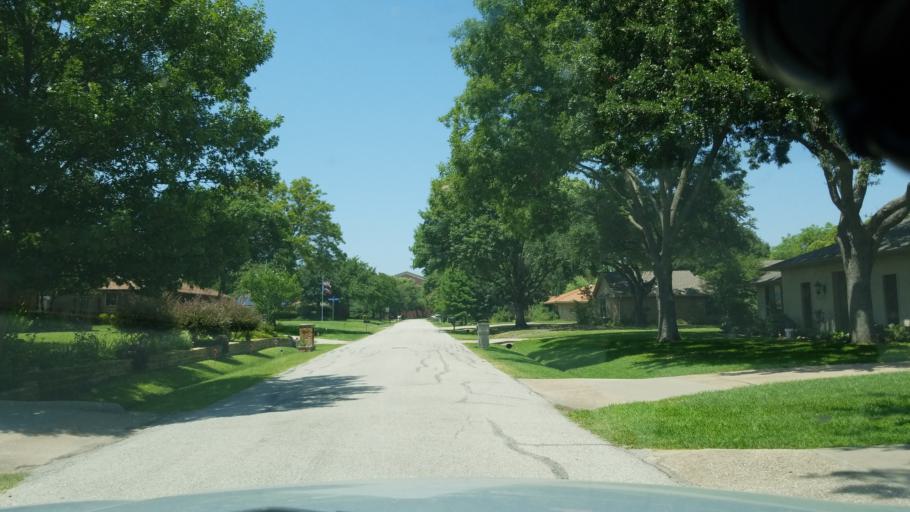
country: US
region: Texas
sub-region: Dallas County
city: Coppell
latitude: 32.9578
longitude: -96.9888
